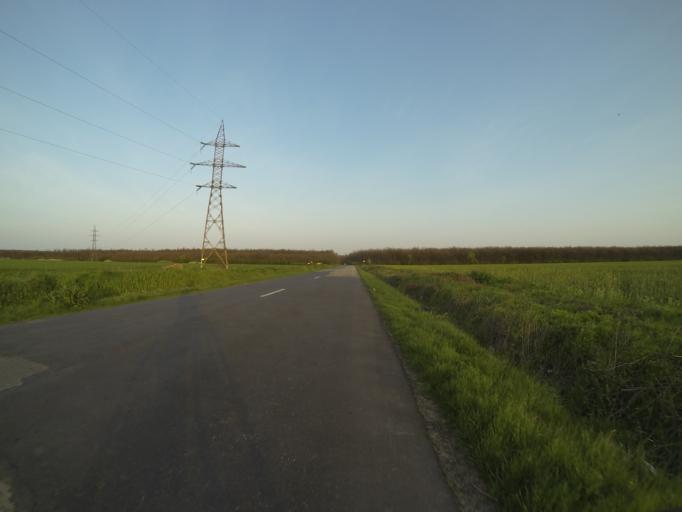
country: RO
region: Dolj
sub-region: Comuna Dranicu
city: Dranic
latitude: 44.0688
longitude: 23.8012
